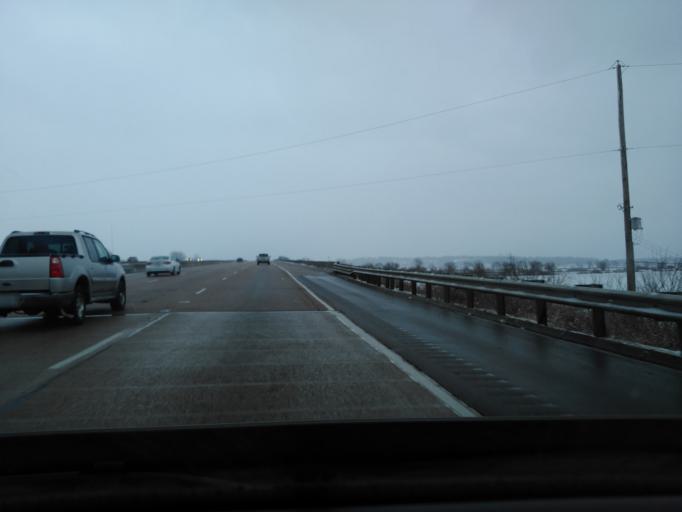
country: US
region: Illinois
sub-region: Saint Clair County
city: Caseyville
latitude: 38.6431
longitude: -90.0477
